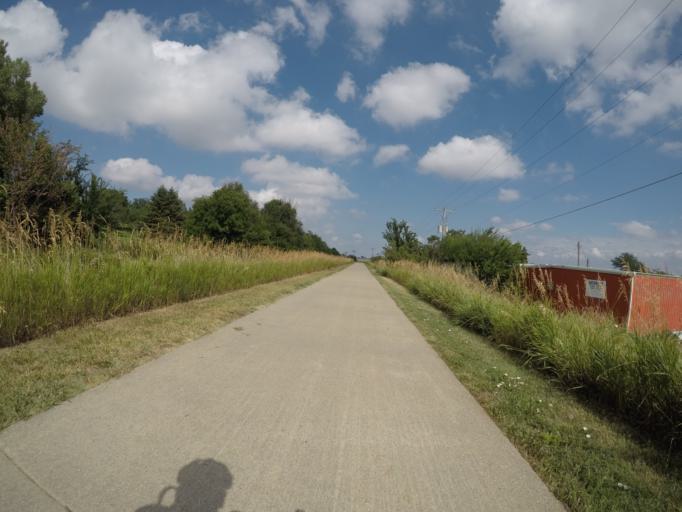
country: US
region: Nebraska
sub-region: Buffalo County
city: Kearney
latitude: 40.7013
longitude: -99.1171
